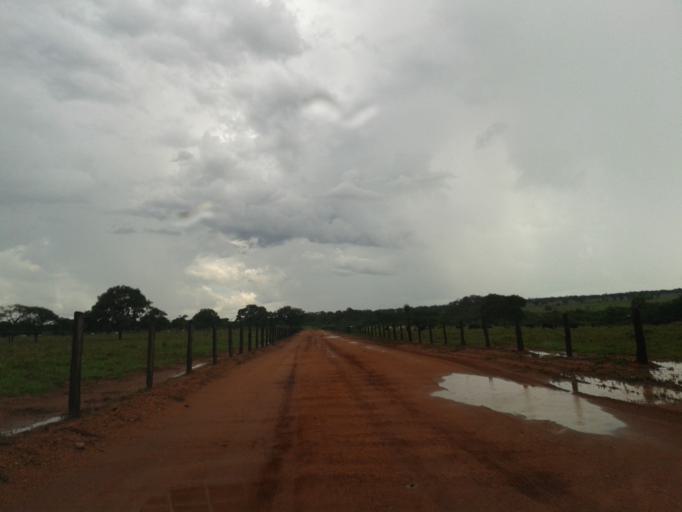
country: BR
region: Minas Gerais
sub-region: Santa Vitoria
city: Santa Vitoria
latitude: -19.1547
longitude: -50.5603
